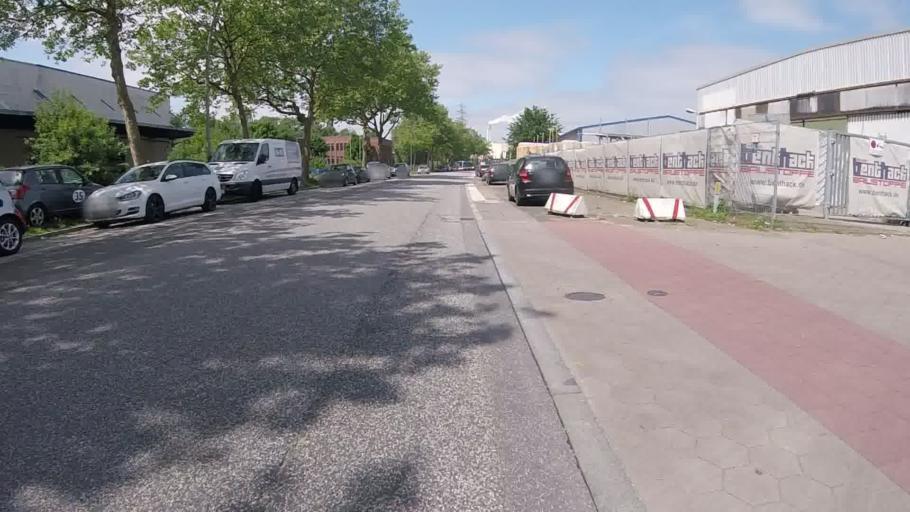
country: DE
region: Hamburg
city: Marienthal
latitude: 53.5258
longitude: 10.0809
